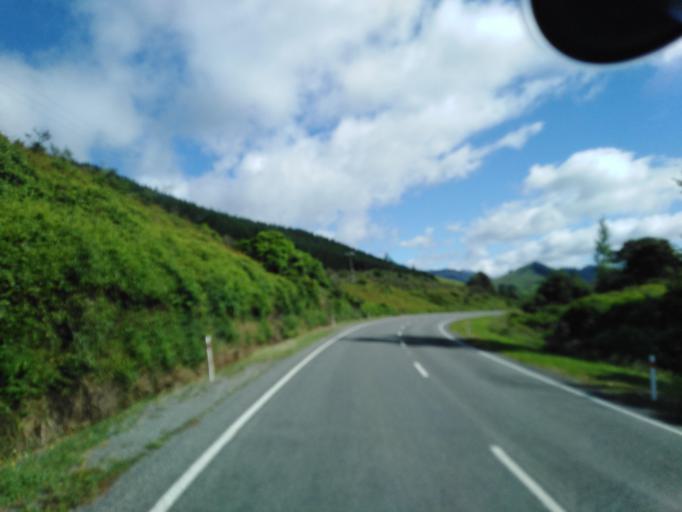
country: NZ
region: Nelson
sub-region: Nelson City
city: Nelson
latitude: -41.2464
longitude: 173.5768
